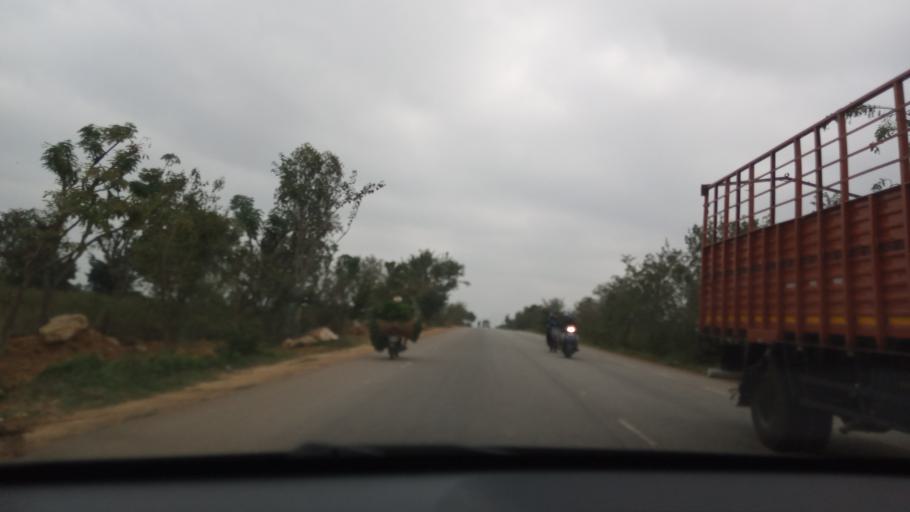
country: IN
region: Karnataka
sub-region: Chikkaballapur
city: Sidlaghatta
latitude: 13.2695
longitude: 77.9490
